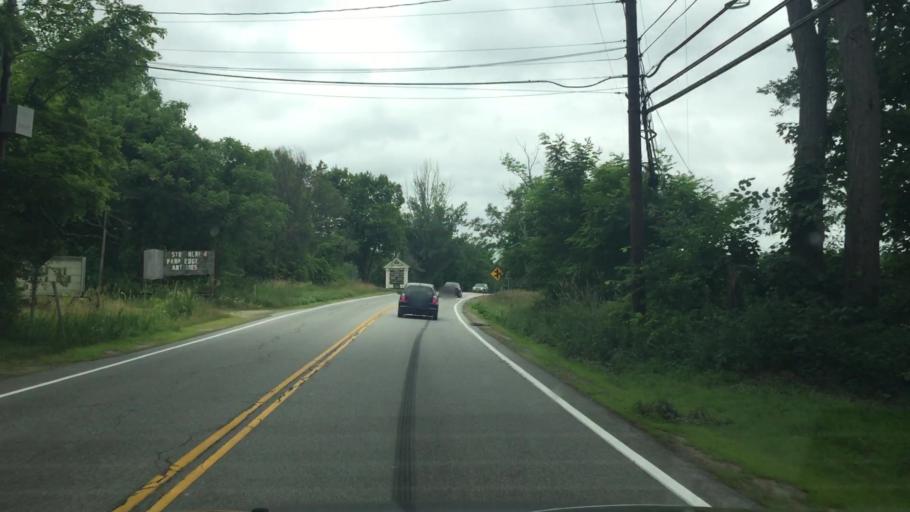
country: US
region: New Hampshire
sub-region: Belknap County
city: Meredith
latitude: 43.6715
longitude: -71.4865
